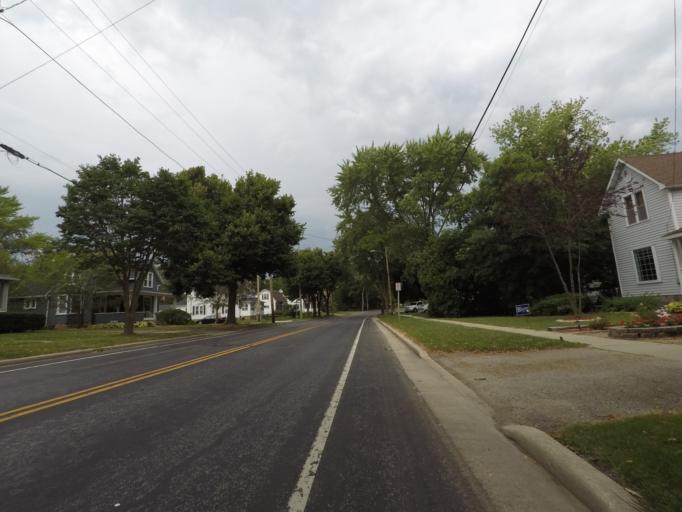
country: US
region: Wisconsin
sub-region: Jefferson County
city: Fort Atkinson
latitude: 42.9368
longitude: -88.8384
